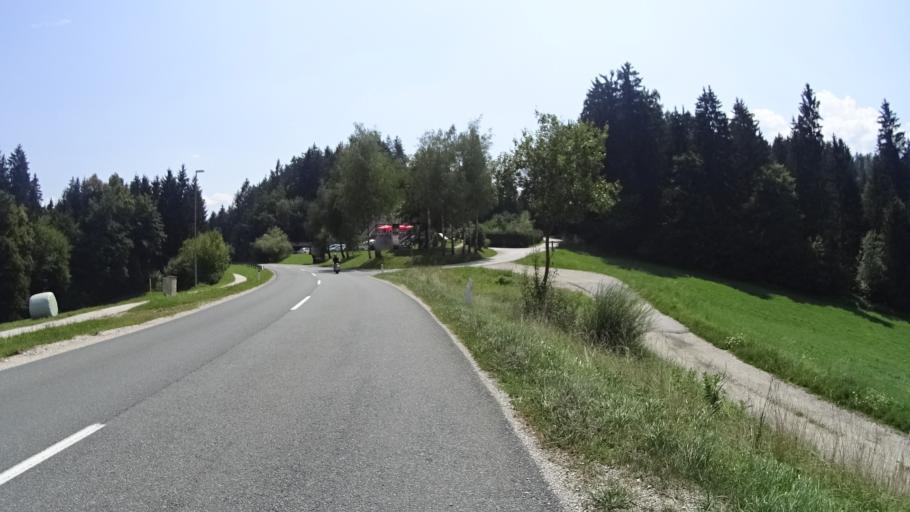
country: SI
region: Mezica
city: Mezica
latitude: 46.5606
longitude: 14.8485
